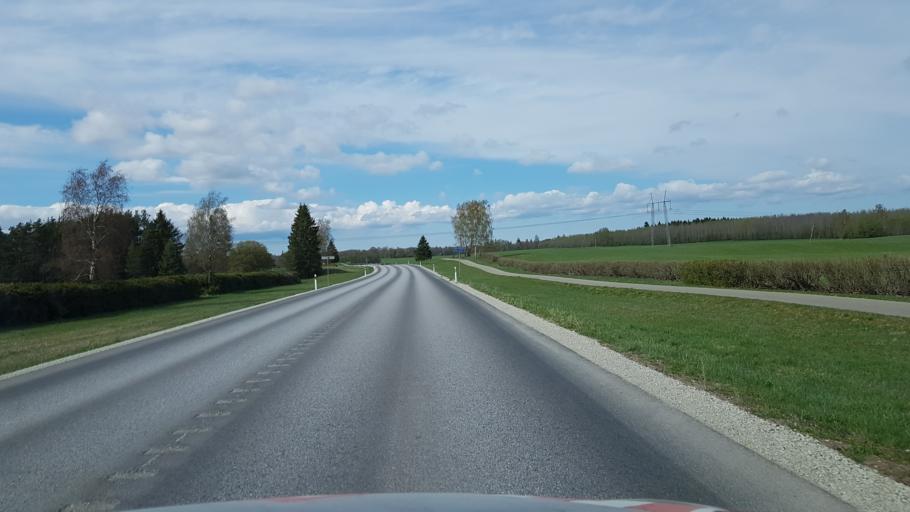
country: EE
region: Laeaene-Virumaa
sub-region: Vinni vald
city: Vinni
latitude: 59.2731
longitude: 26.4361
